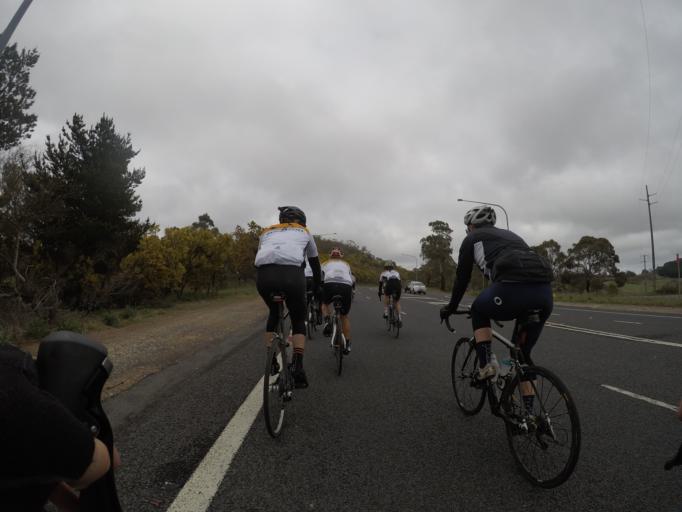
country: AU
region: New South Wales
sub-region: Lithgow
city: Portland
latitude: -33.4539
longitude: 149.9876
